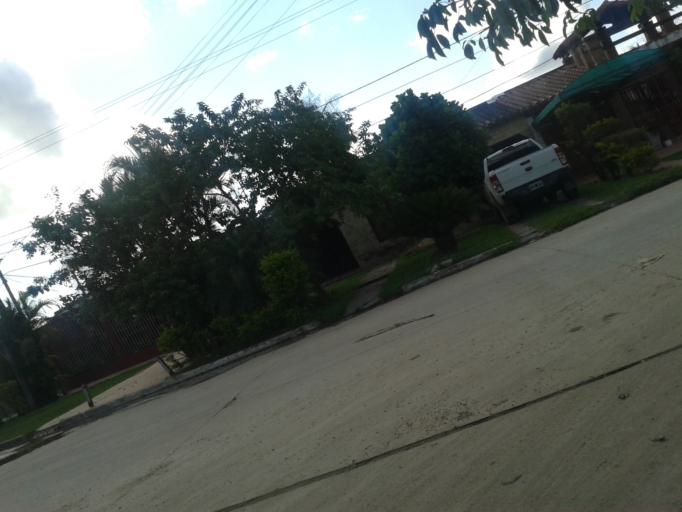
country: AR
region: Formosa
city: Clorinda
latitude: -25.2827
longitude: -57.7380
